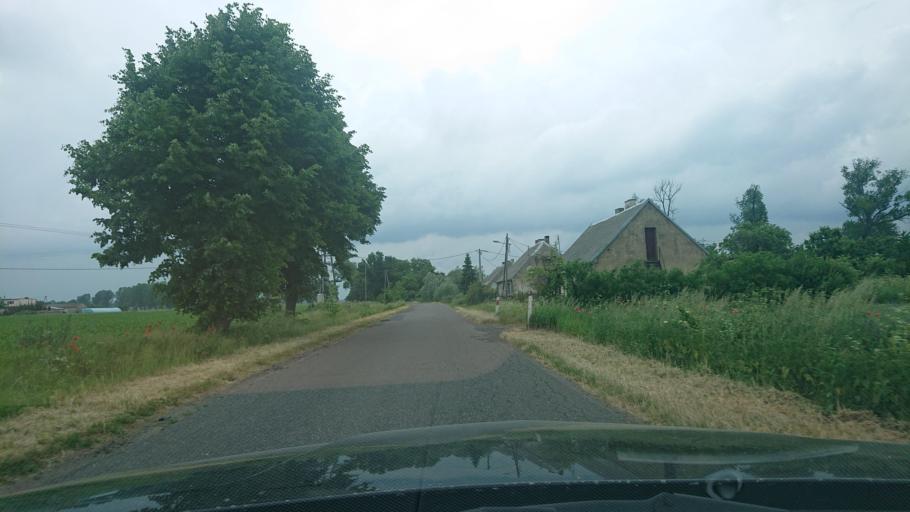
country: PL
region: Greater Poland Voivodeship
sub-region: Powiat gnieznienski
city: Czerniejewo
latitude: 52.4677
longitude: 17.5223
